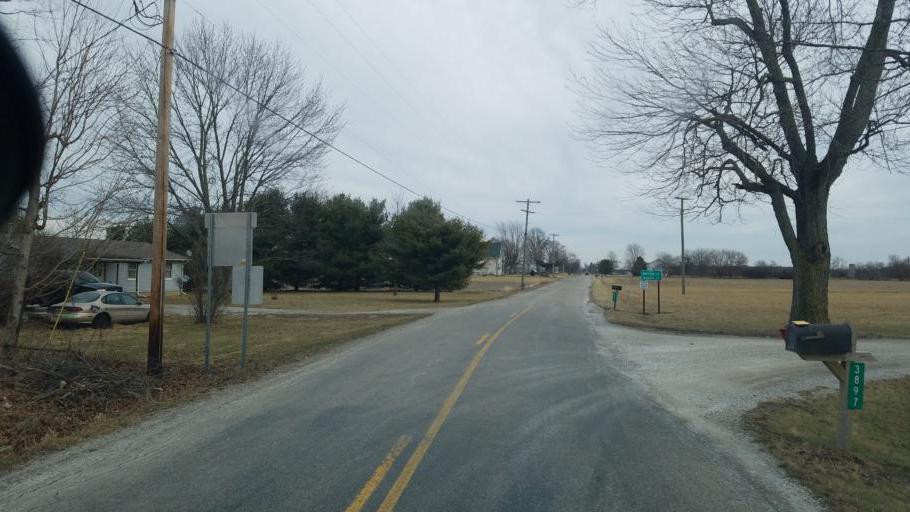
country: US
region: Ohio
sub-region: Delaware County
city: Ashley
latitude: 40.4565
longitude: -83.0193
